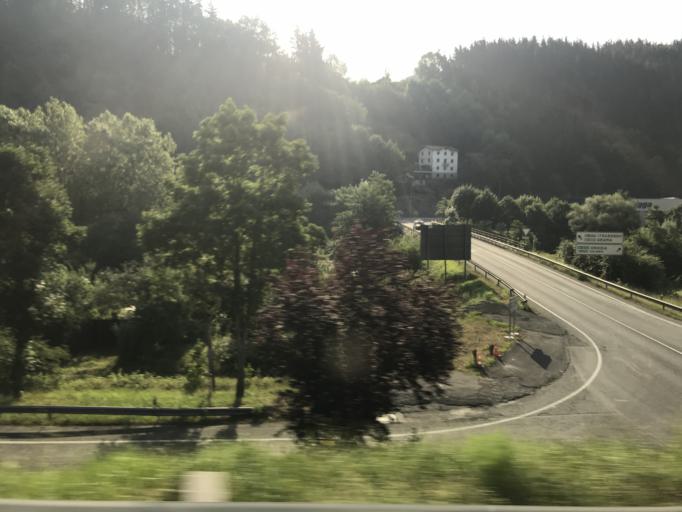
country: ES
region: Basque Country
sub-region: Provincia de Guipuzcoa
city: Arama
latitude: 43.0598
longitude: -2.1710
